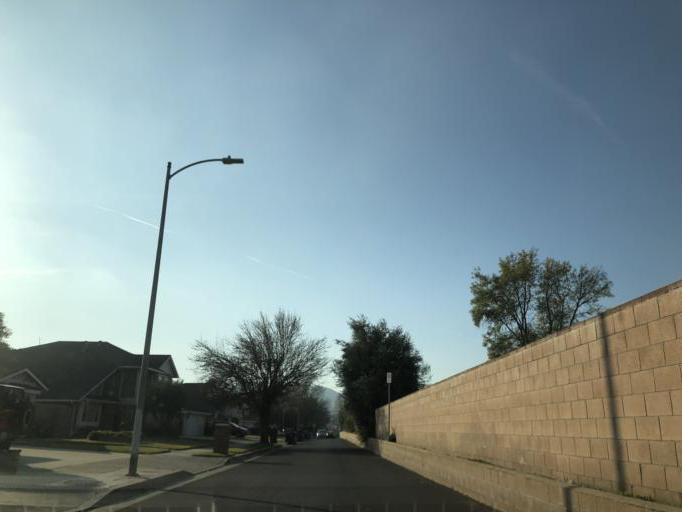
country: US
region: California
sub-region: Los Angeles County
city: Chatsworth
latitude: 34.2607
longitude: -118.5805
